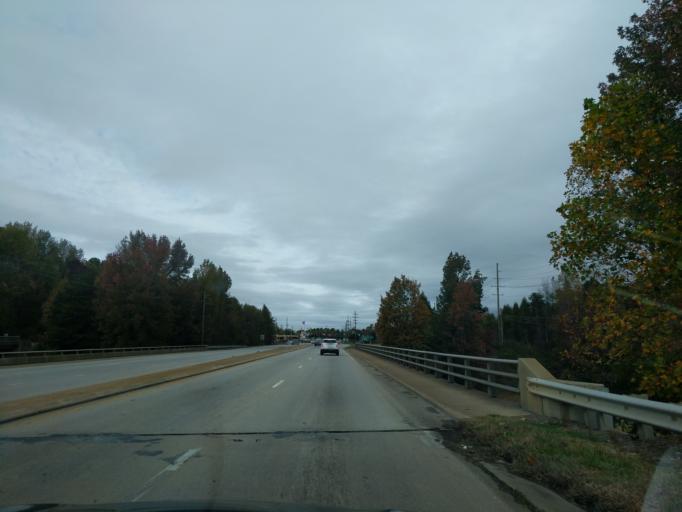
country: US
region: North Carolina
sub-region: Davidson County
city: Lexington
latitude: 35.7797
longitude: -80.2598
